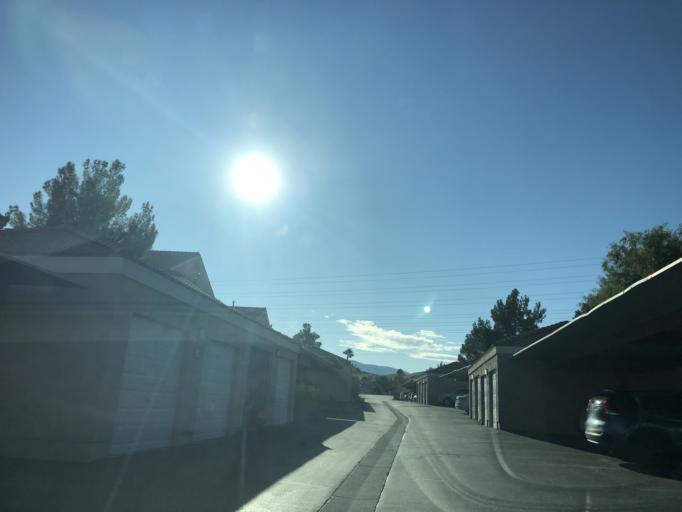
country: US
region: Nevada
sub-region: Clark County
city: Whitney
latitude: 36.0038
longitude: -115.0947
